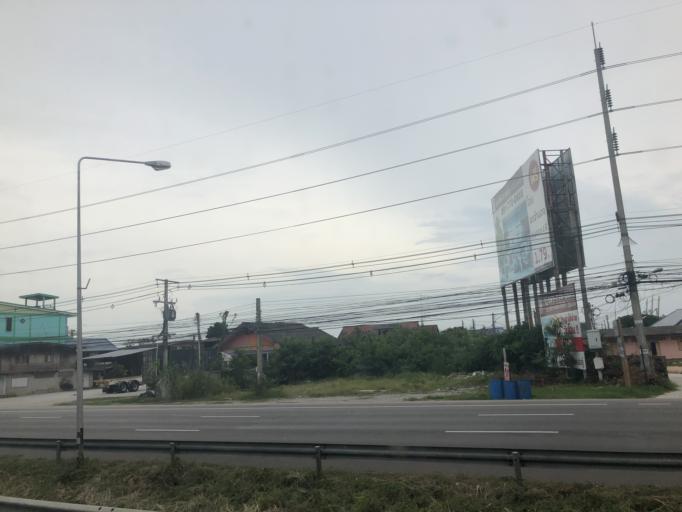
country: TH
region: Chon Buri
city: Bang Lamung
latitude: 13.0528
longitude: 100.9261
